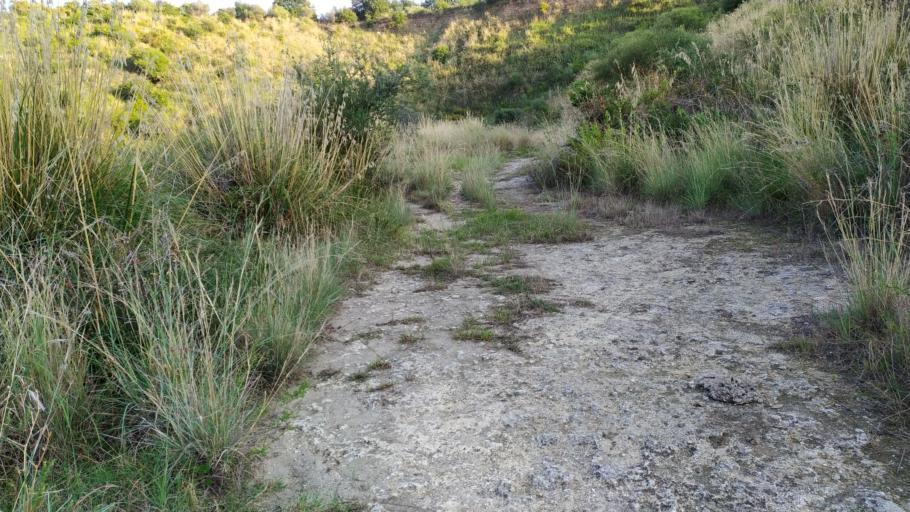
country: IT
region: Sicily
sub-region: Messina
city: Saponara Marittima
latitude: 38.2246
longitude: 15.4319
